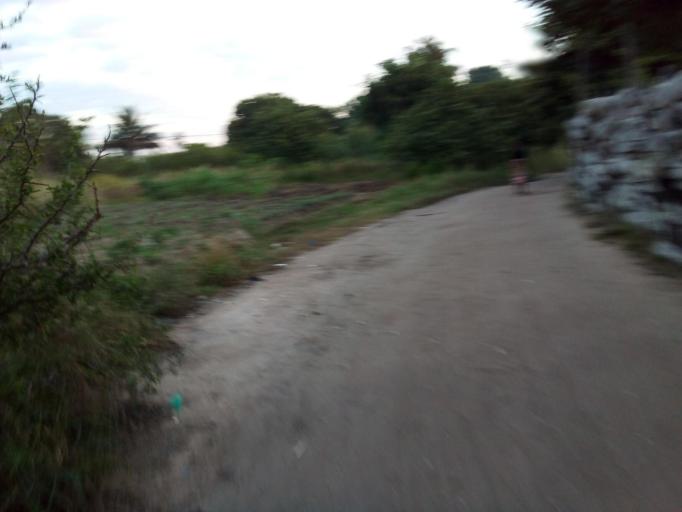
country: MZ
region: Zambezia
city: Quelimane
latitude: -17.6038
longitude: 36.8148
